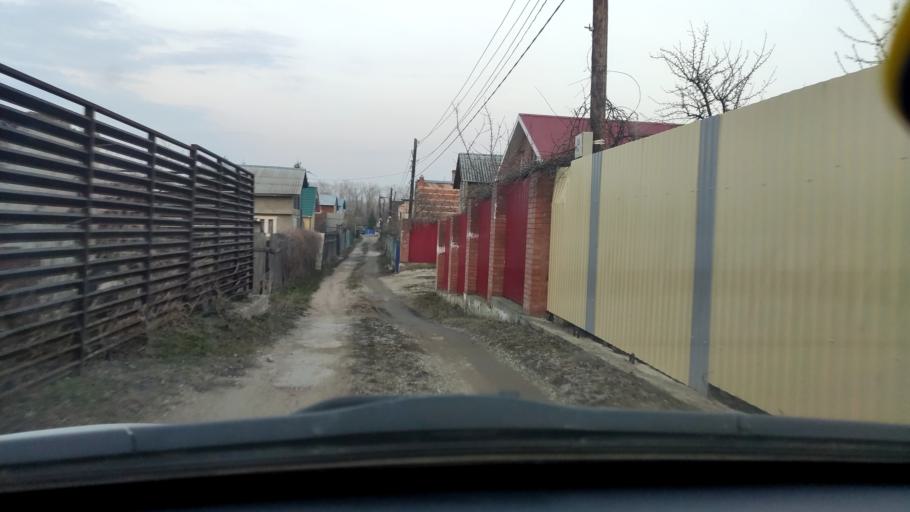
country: RU
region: Samara
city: Zhigulevsk
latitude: 53.4528
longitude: 49.5233
